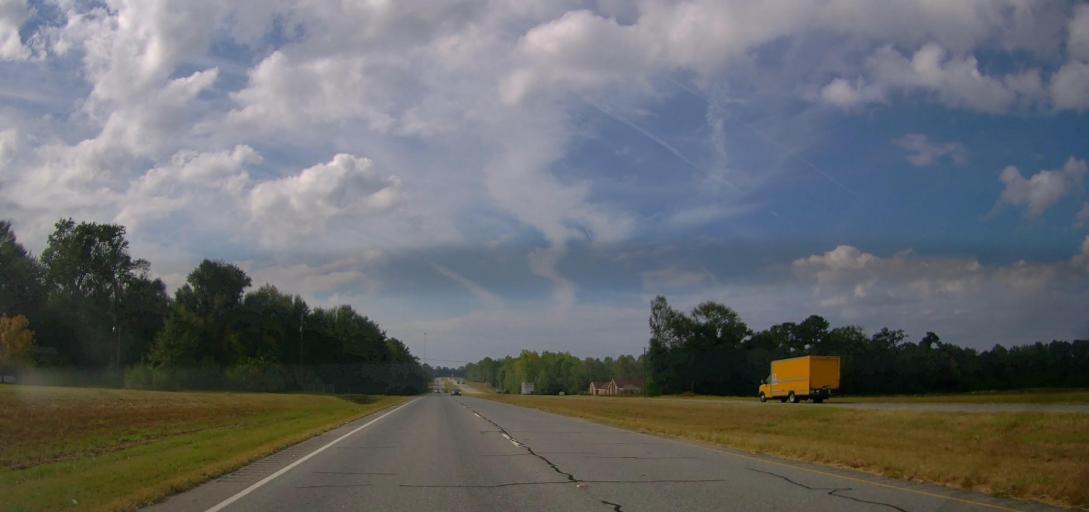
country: US
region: Georgia
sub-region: Mitchell County
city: Pelham
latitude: 31.1130
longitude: -84.1266
